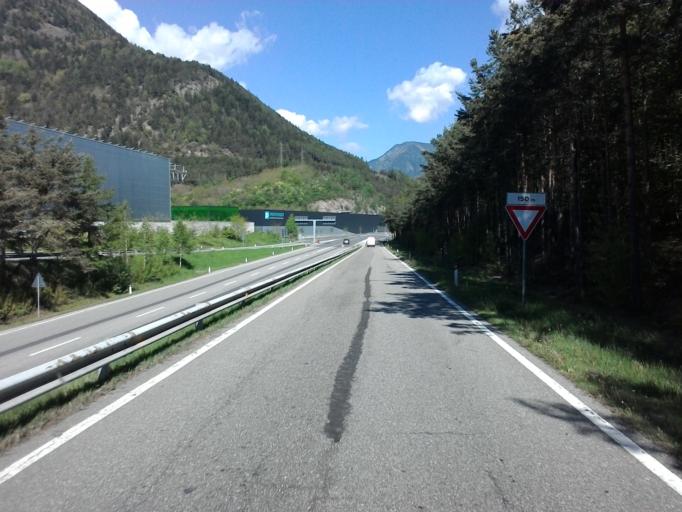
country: IT
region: Trentino-Alto Adige
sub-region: Bolzano
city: Naz-Sciaves - Natz-Schabs
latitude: 46.7661
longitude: 11.6423
